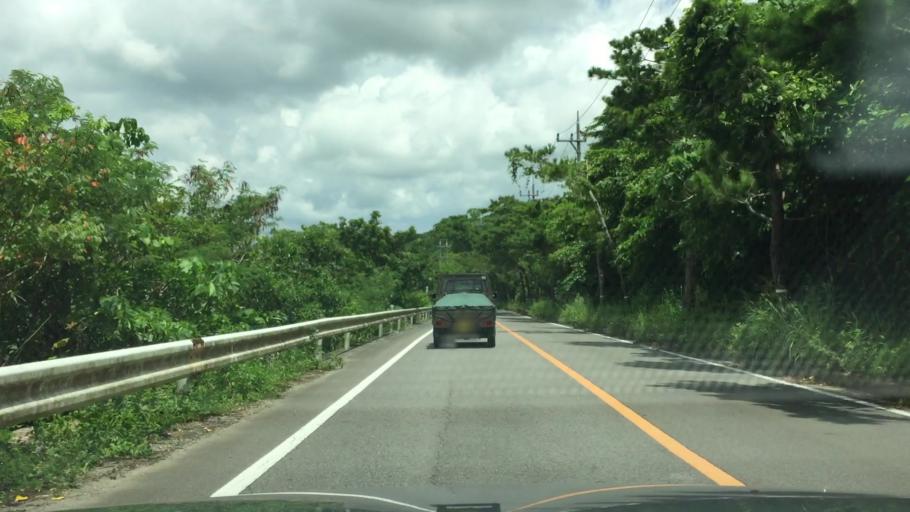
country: JP
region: Okinawa
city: Ishigaki
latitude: 24.3792
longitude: 124.1538
